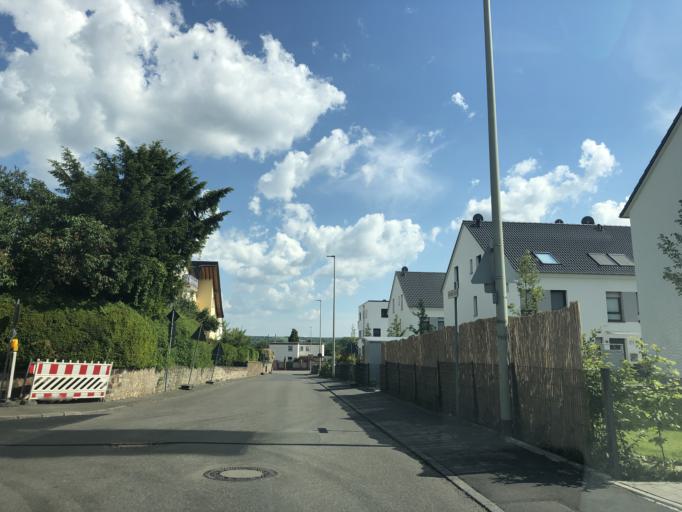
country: DE
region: Hesse
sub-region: Regierungsbezirk Darmstadt
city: Eltville
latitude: 50.0246
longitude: 8.1130
